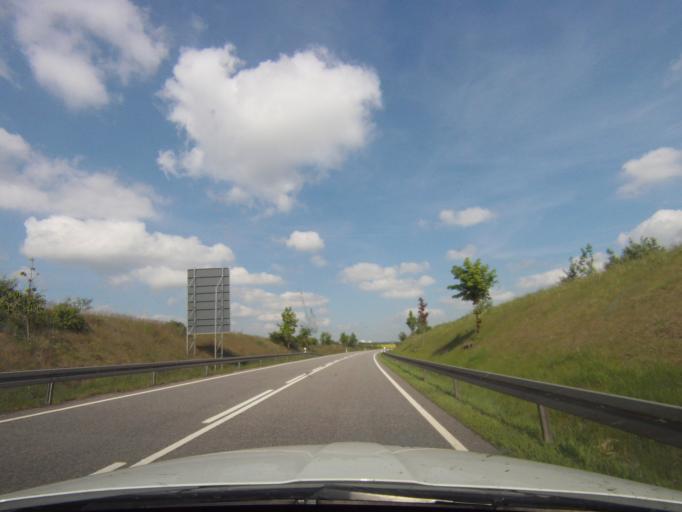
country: DE
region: Thuringia
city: Mittelpollnitz
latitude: 50.7581
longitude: 11.9096
